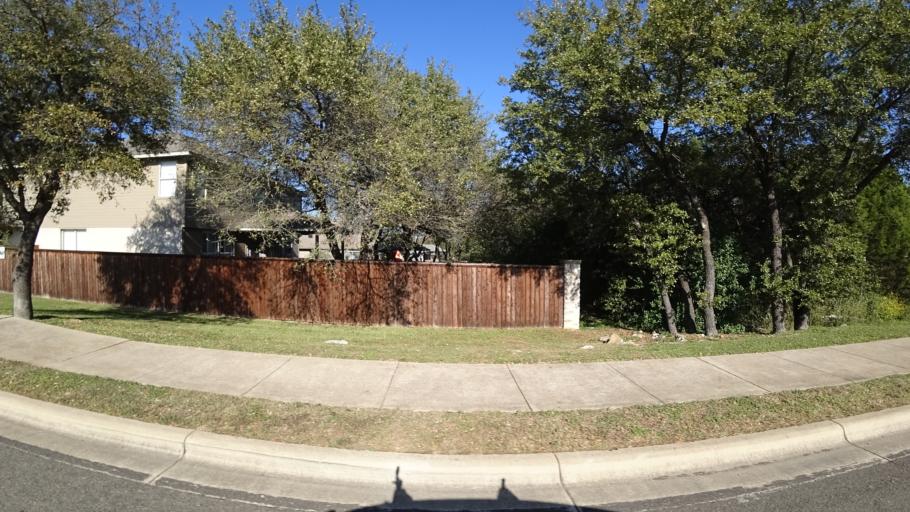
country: US
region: Texas
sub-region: Travis County
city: Shady Hollow
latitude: 30.2014
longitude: -97.8571
